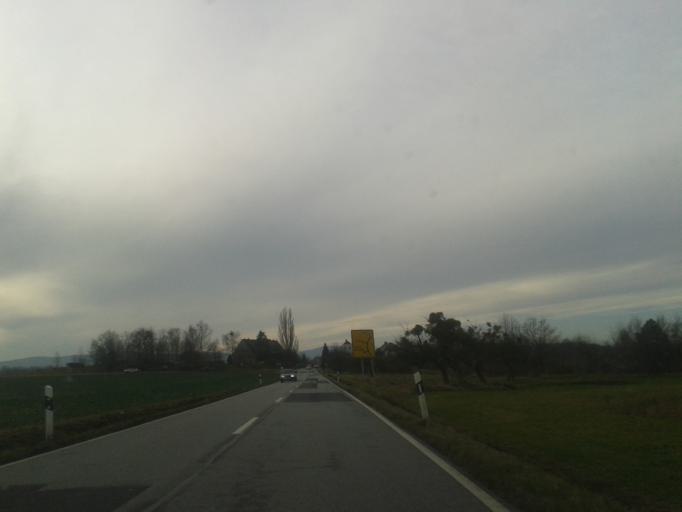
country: DE
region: Saxony
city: Weissenberg
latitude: 51.1899
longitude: 14.6451
